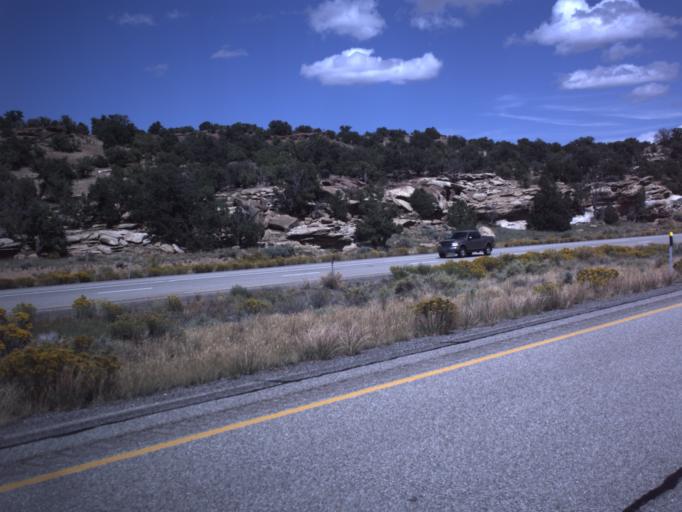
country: US
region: Utah
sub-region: Emery County
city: Castle Dale
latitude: 38.8745
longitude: -110.7514
